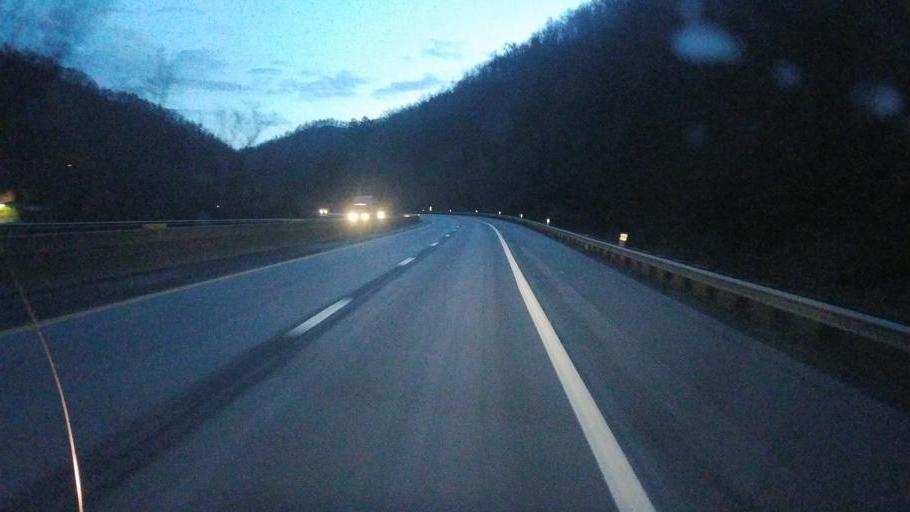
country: US
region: West Virginia
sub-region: Kanawha County
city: Montgomery
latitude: 38.0802
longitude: -81.3810
